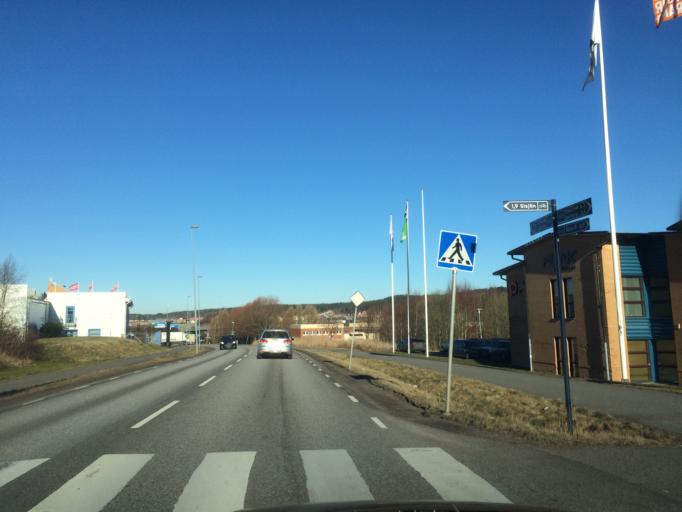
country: SE
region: Vaestra Goetaland
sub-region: Molndal
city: Moelndal
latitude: 57.6423
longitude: 11.9908
